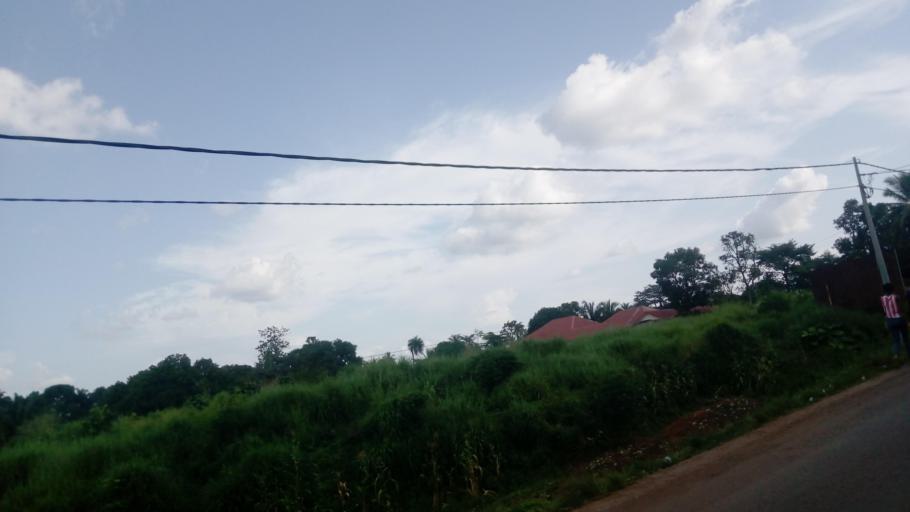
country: SL
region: Northern Province
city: Makeni
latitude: 8.8987
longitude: -12.0372
